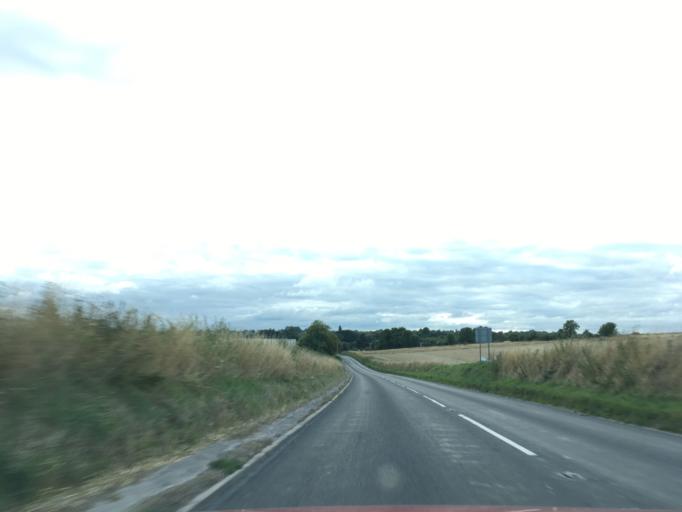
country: GB
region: England
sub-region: Wiltshire
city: Devizes
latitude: 51.3381
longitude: -1.9612
